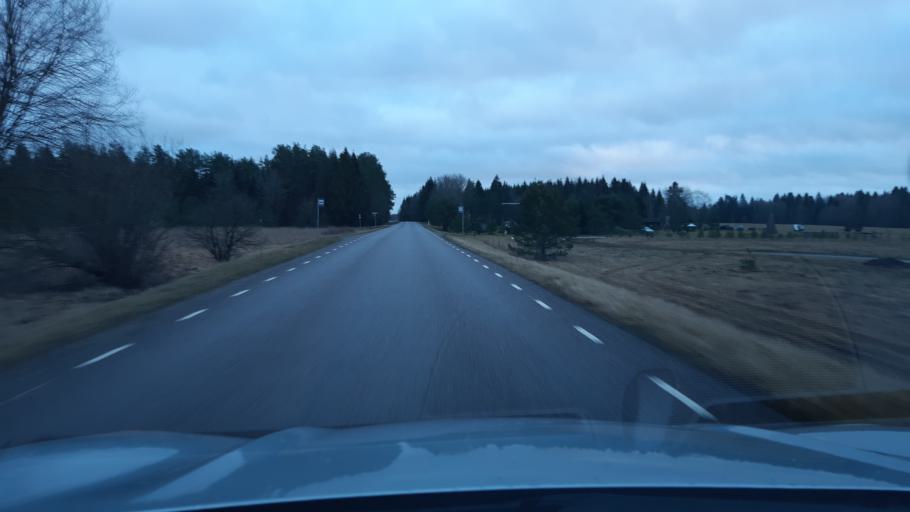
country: EE
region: Raplamaa
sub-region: Kohila vald
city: Kohila
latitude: 59.1284
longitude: 24.6686
